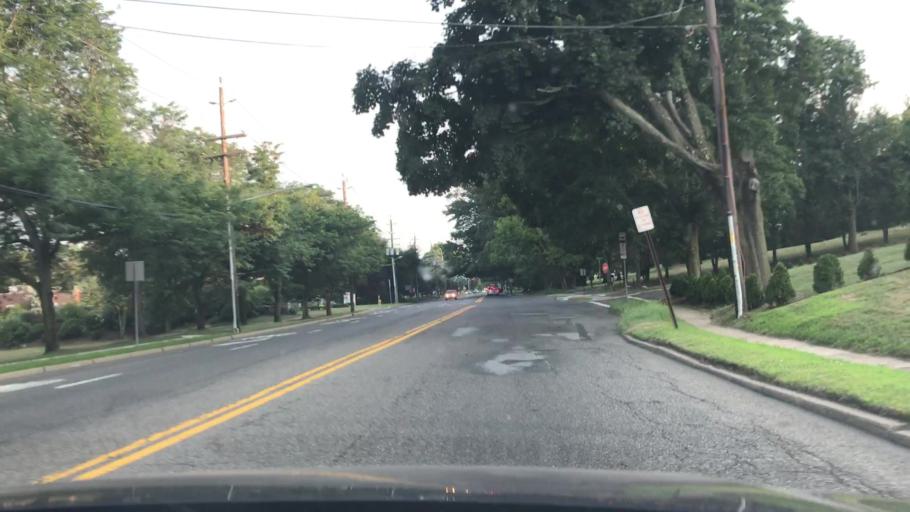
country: US
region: New Jersey
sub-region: Bergen County
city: Oradell
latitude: 40.9633
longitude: -74.0307
